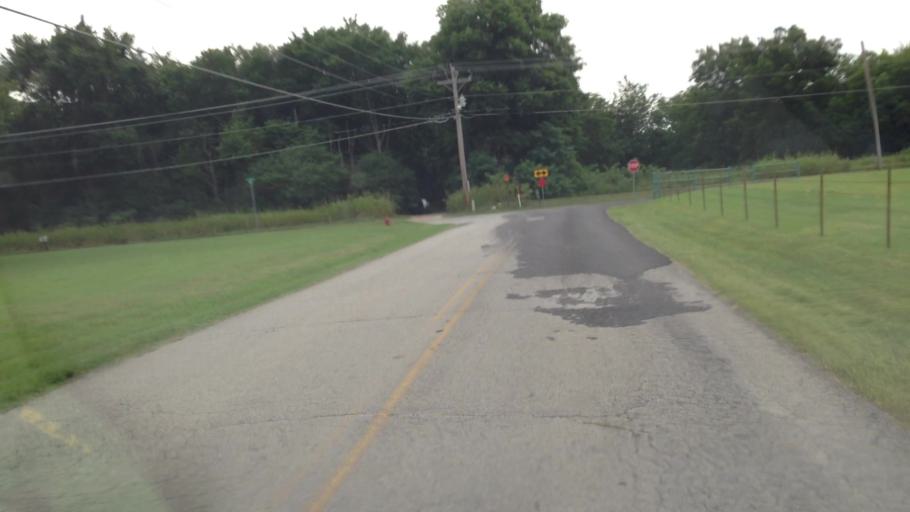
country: US
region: Oklahoma
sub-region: Delaware County
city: Cleora
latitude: 36.5531
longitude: -94.9617
